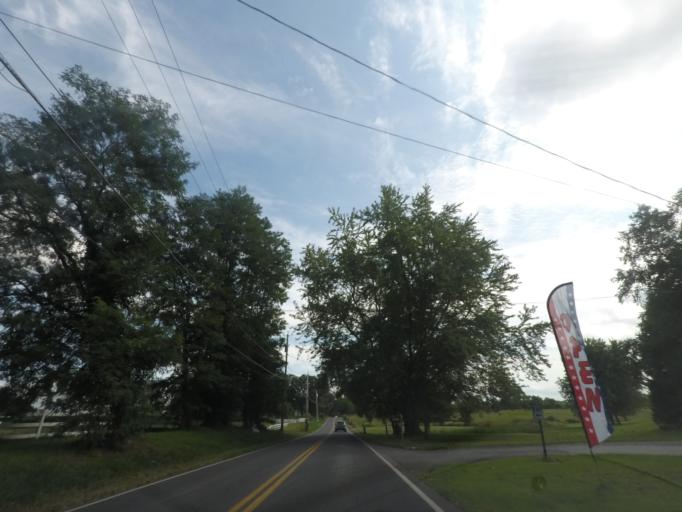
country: US
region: New York
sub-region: Albany County
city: Delmar
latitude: 42.6209
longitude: -73.8018
